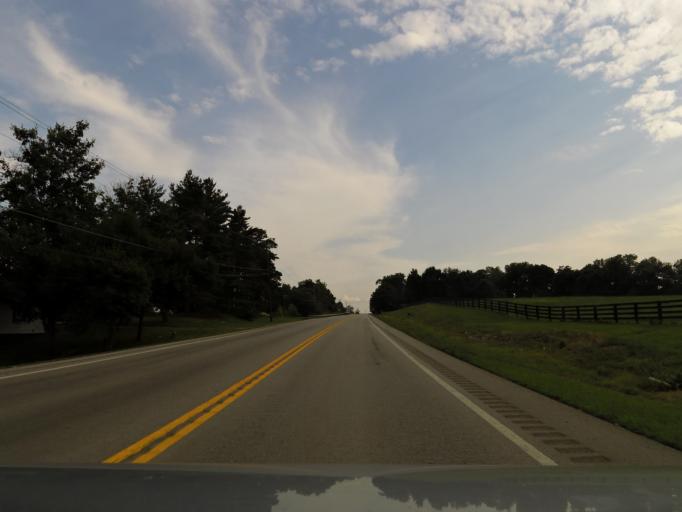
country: US
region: Kentucky
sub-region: Harrison County
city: Cynthiana
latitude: 38.4157
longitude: -84.2830
